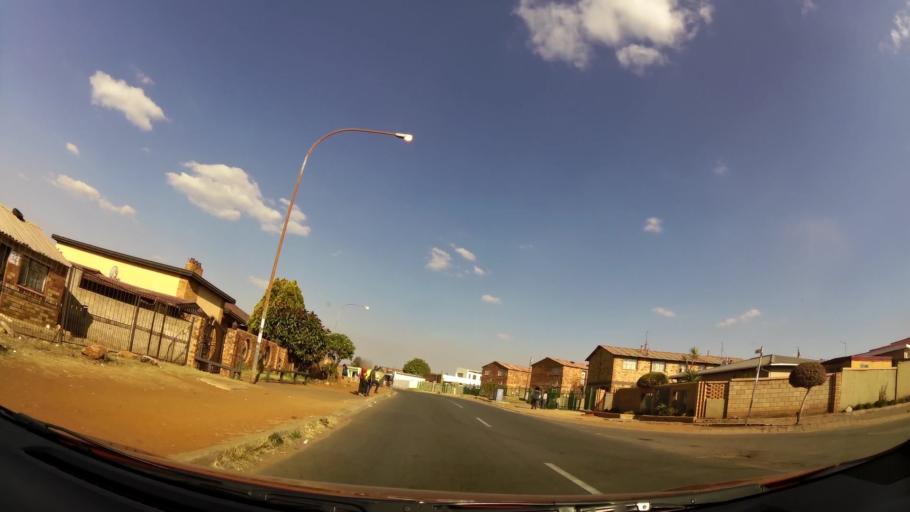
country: ZA
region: Gauteng
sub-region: City of Johannesburg Metropolitan Municipality
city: Soweto
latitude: -26.2287
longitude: 27.8745
